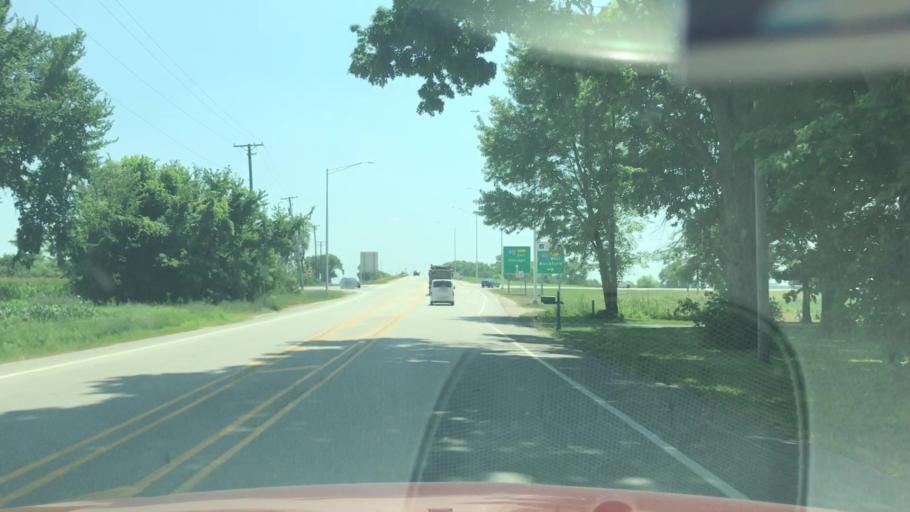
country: US
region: Illinois
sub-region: Winnebago County
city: Cherry Valley
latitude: 42.2366
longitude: -88.9007
